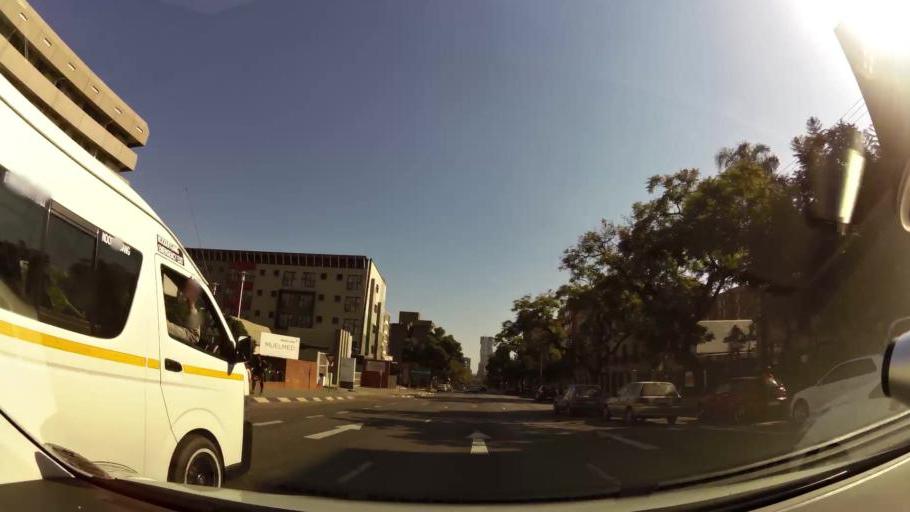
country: ZA
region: Gauteng
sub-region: City of Tshwane Metropolitan Municipality
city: Pretoria
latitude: -25.7467
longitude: 28.2074
